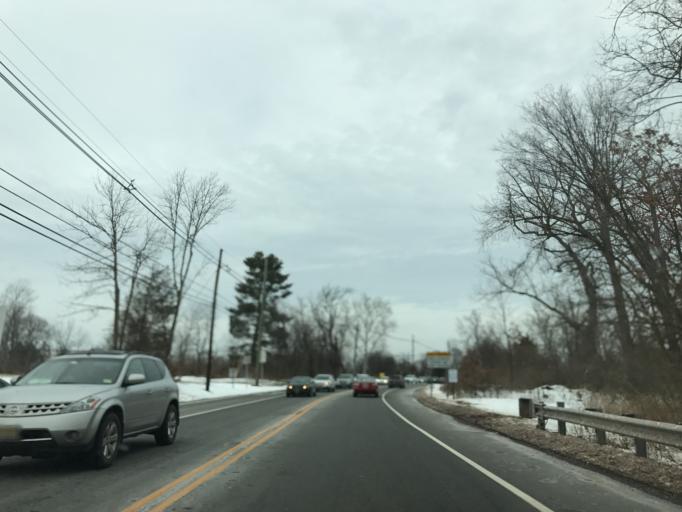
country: US
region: New Jersey
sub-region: Somerset County
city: Bloomingdale
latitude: 40.5275
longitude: -74.6267
